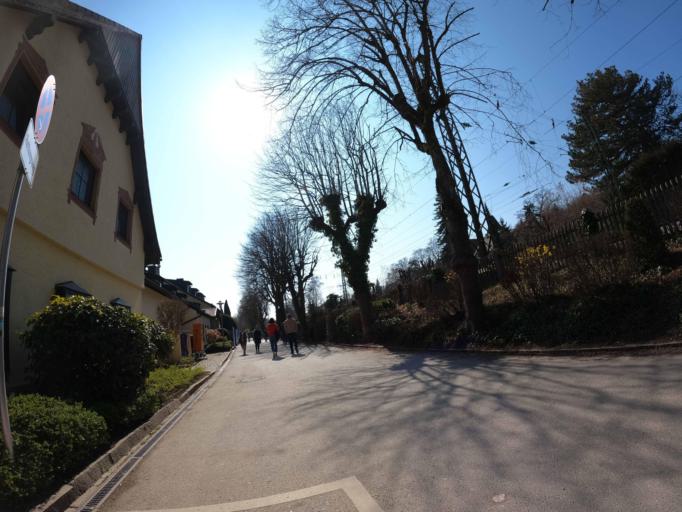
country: DE
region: Bavaria
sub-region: Upper Bavaria
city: Starnberg
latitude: 47.9946
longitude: 11.3403
